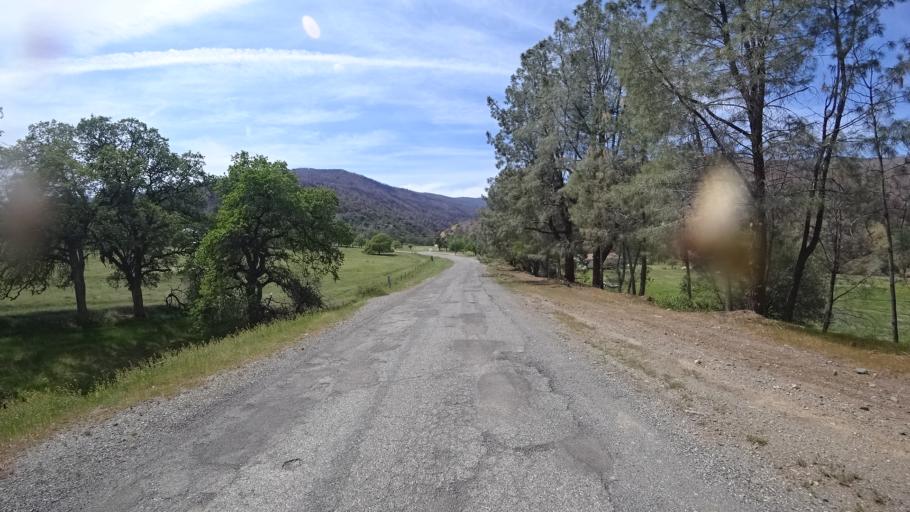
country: US
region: California
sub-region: Glenn County
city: Willows
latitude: 39.5752
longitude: -122.6123
